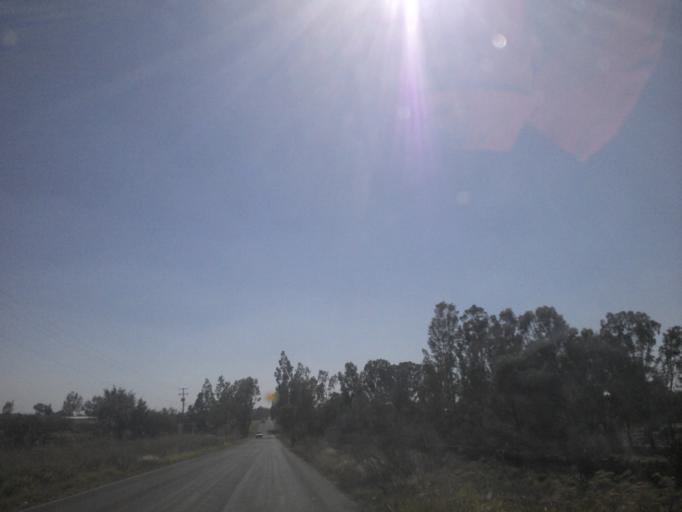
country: MX
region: Jalisco
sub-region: Arandas
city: Santiaguito (Santiaguito de Velazquez)
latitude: 20.8336
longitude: -102.1125
